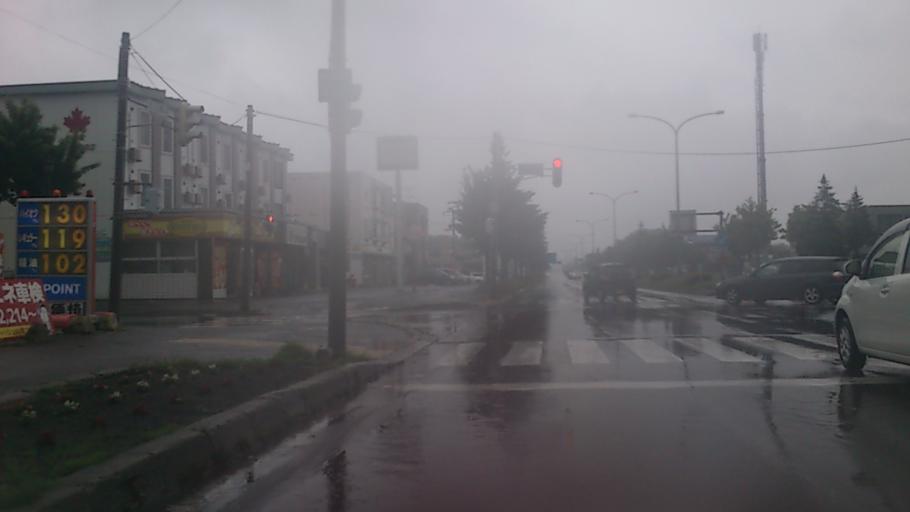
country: JP
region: Hokkaido
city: Obihiro
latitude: 42.9115
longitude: 143.1314
